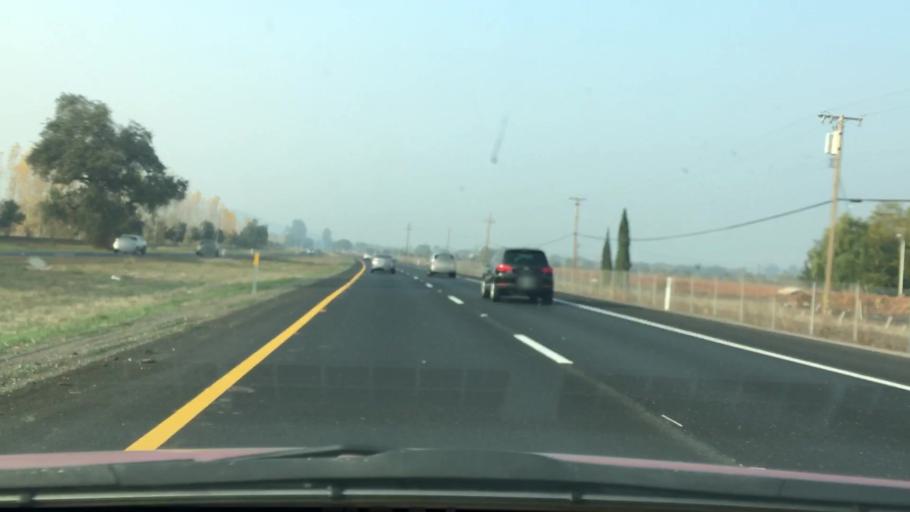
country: US
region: California
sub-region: Napa County
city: Yountville
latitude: 38.3765
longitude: -122.3436
